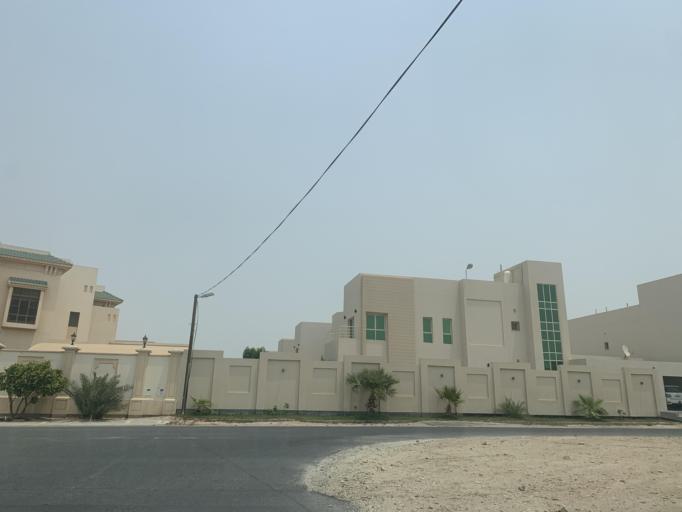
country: BH
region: Central Governorate
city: Madinat Hamad
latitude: 26.1697
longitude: 50.4787
